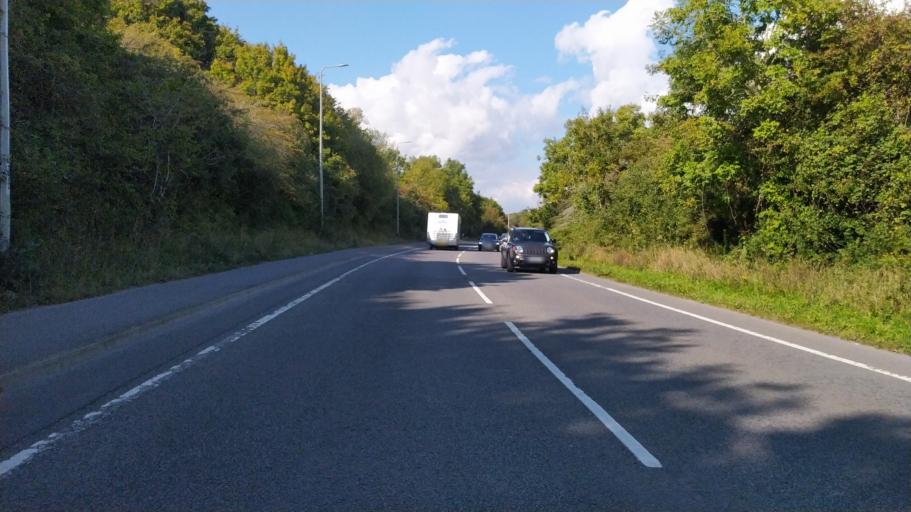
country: GB
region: England
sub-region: Dorset
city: Weymouth
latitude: 50.6263
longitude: -2.4722
